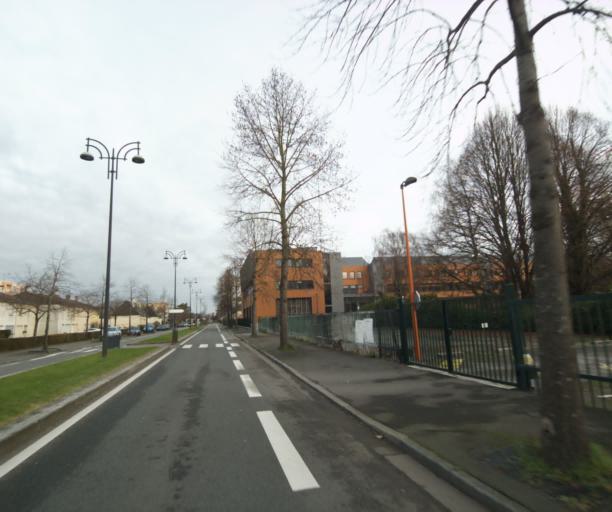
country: FR
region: Pays de la Loire
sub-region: Departement de la Sarthe
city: Coulaines
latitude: 48.0196
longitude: 0.2016
